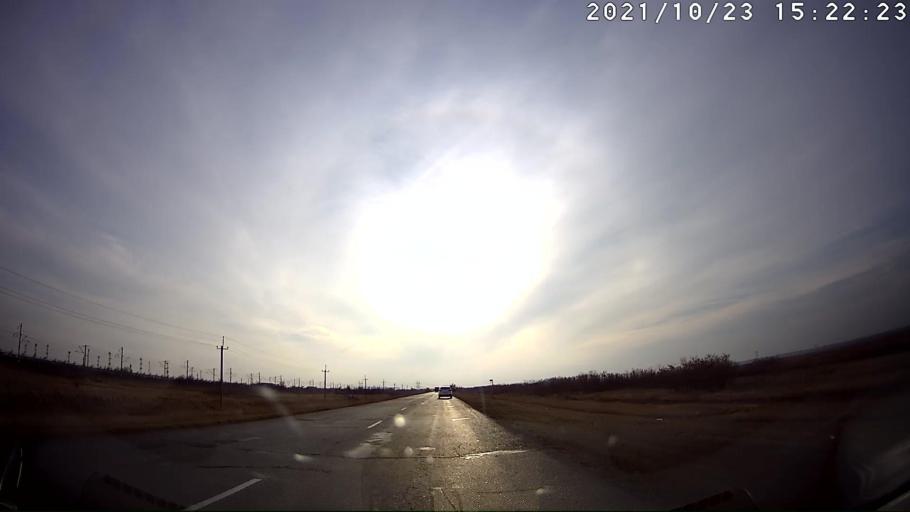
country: RU
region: Volgograd
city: Bereslavka
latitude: 48.3048
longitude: 44.2988
